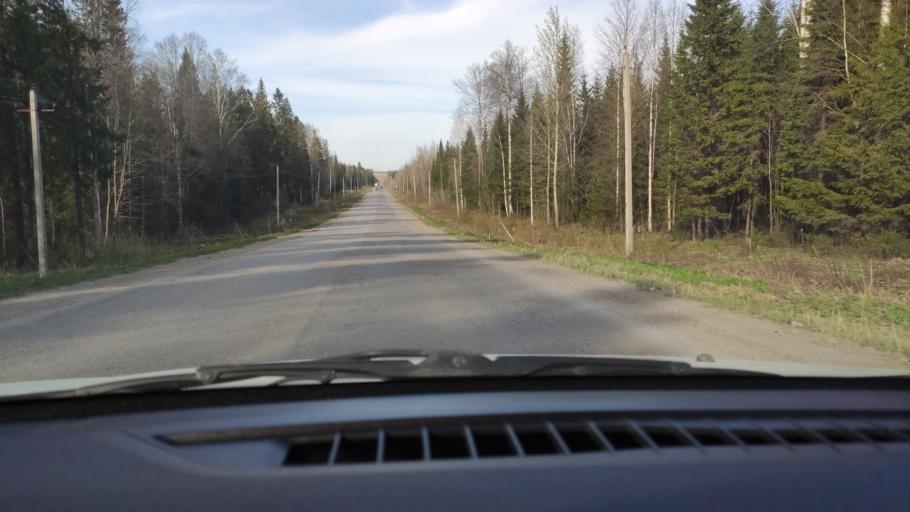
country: RU
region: Perm
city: Novyye Lyady
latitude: 57.9428
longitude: 56.4982
